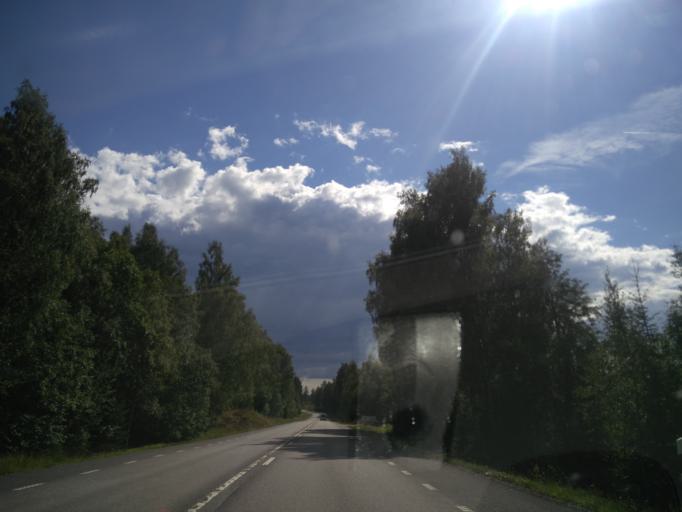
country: SE
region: OErebro
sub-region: Hallefors Kommun
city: Haellefors
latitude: 59.7561
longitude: 14.5122
